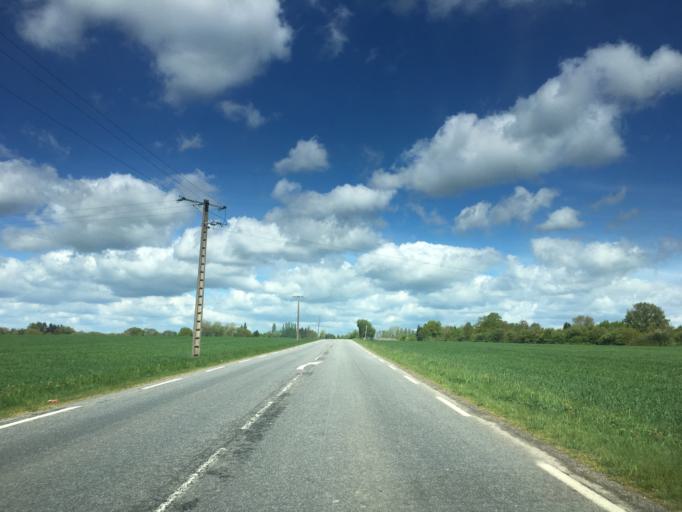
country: FR
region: Lower Normandy
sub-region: Departement de l'Orne
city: Rai
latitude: 48.8211
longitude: 0.5667
